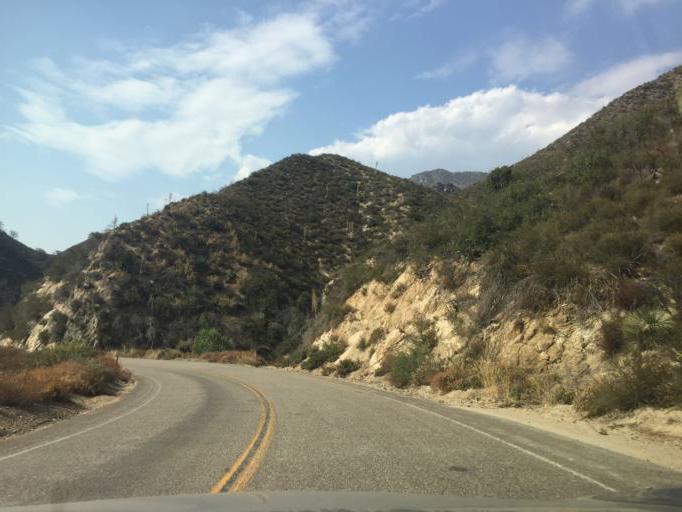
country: US
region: California
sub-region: Los Angeles County
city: Altadena
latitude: 34.2661
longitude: -118.1145
